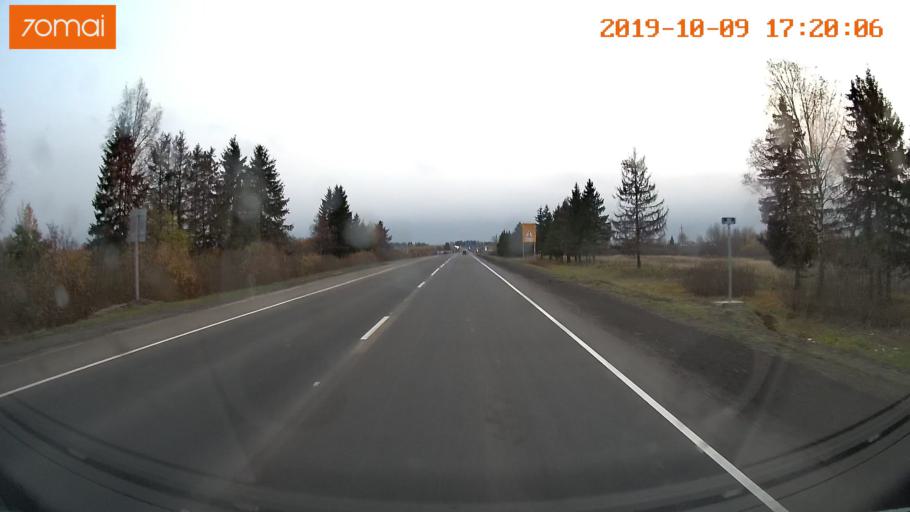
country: RU
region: Ivanovo
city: Furmanov
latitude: 57.2382
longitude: 41.1450
